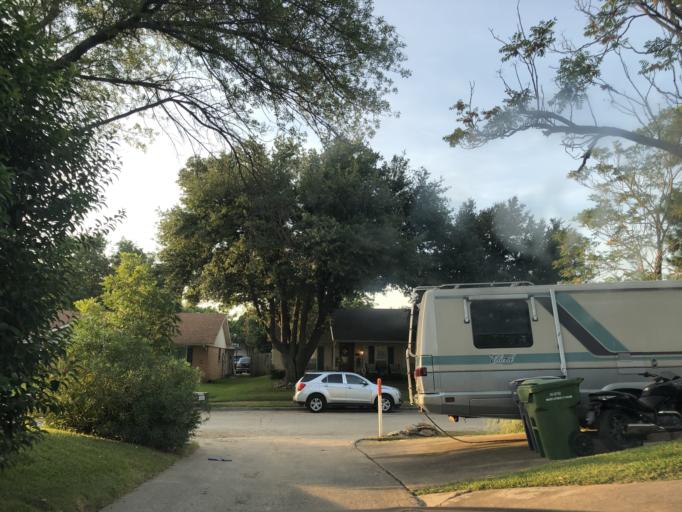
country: US
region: Texas
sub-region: Dallas County
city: Garland
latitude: 32.8625
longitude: -96.6309
